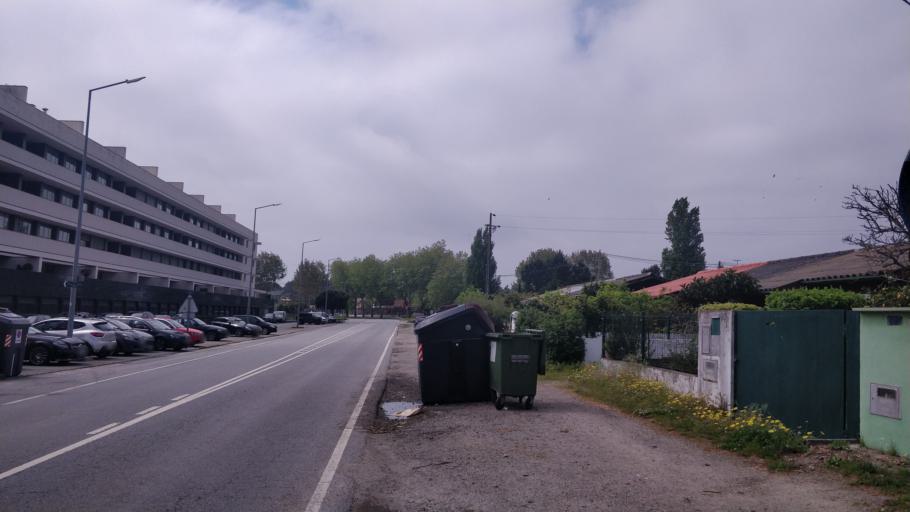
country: PT
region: Viana do Castelo
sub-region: Viana do Castelo
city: Viana do Castelo
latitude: 41.6846
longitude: -8.8203
